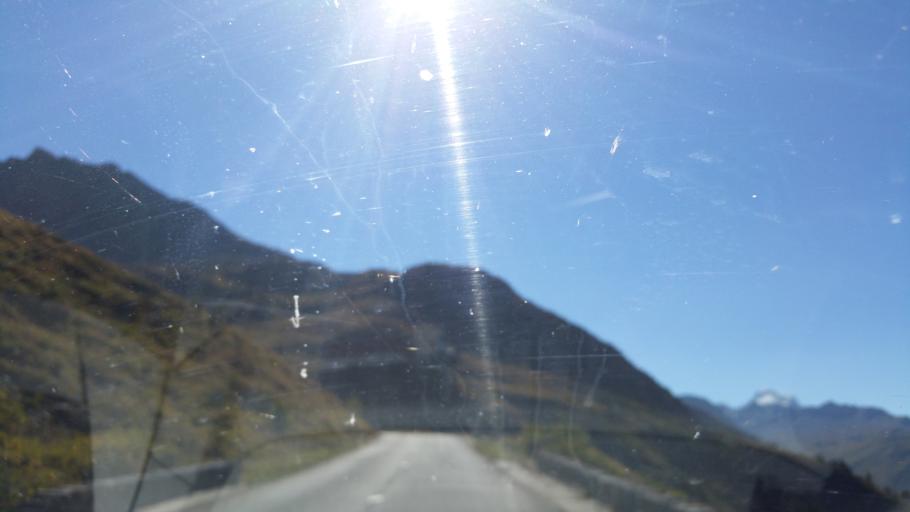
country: FR
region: Rhone-Alpes
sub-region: Departement de la Savoie
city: Val-d'Isere
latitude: 45.4445
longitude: 7.0206
